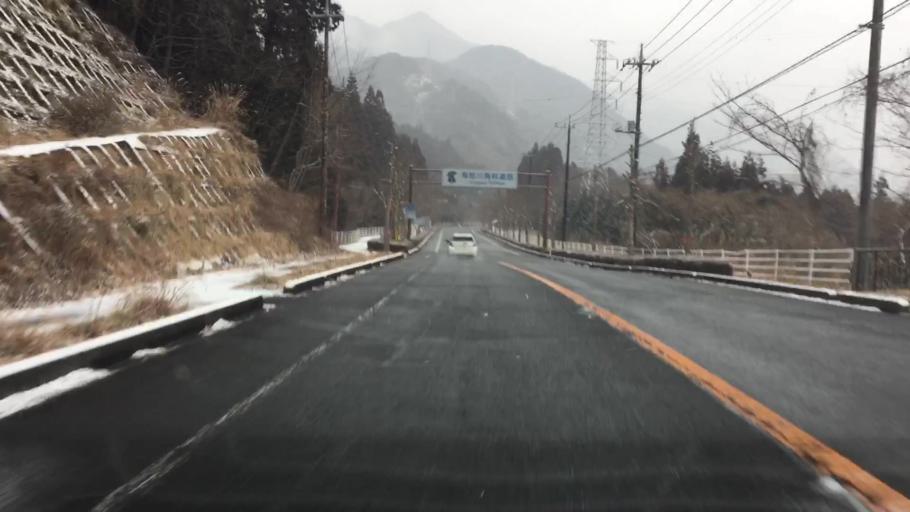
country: JP
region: Tochigi
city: Imaichi
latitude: 36.8126
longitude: 139.7070
